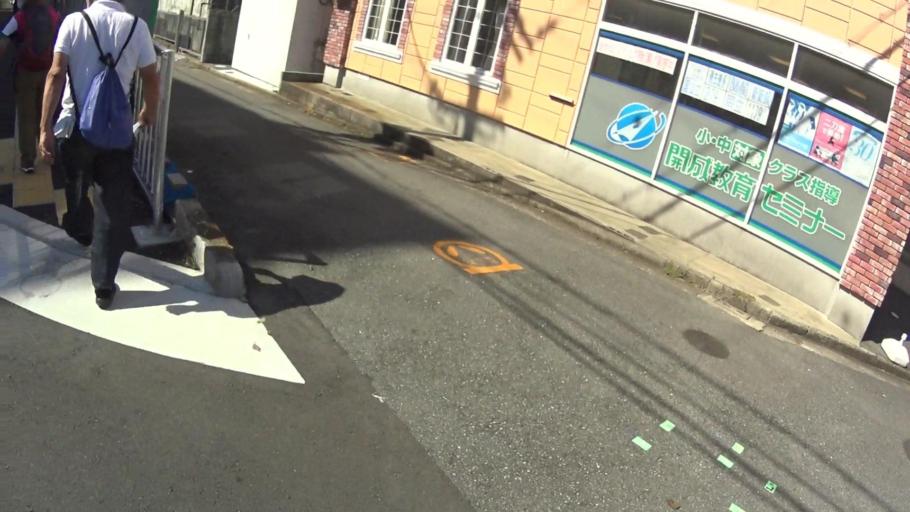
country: JP
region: Osaka
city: Izumiotsu
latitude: 34.4841
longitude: 135.3958
